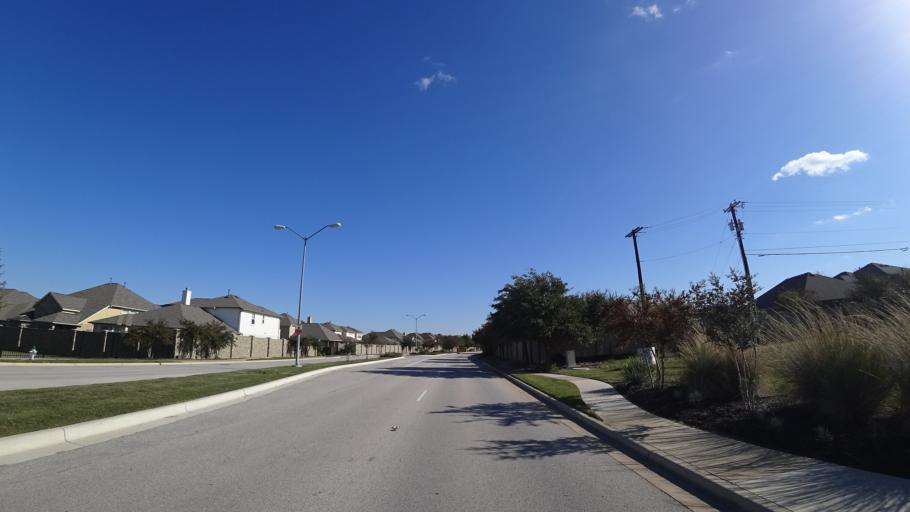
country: US
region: Texas
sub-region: Williamson County
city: Brushy Creek
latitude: 30.4926
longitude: -97.7243
